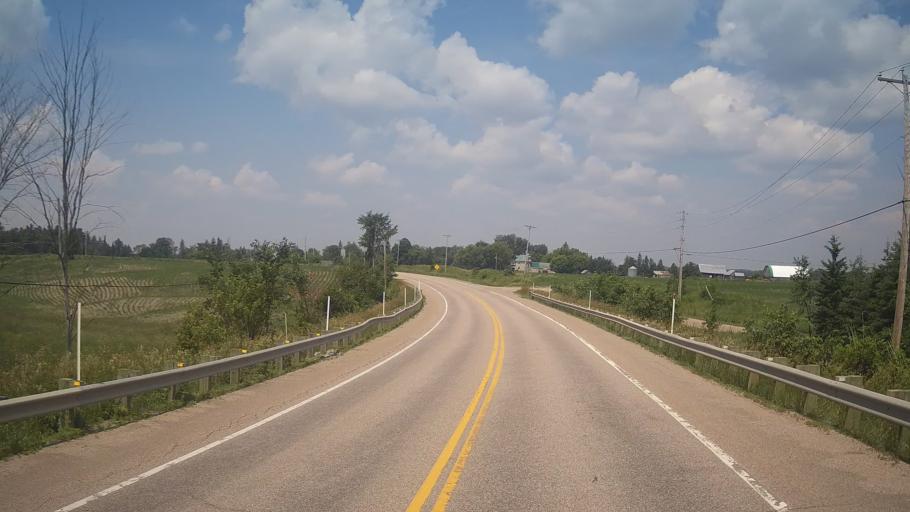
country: CA
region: Quebec
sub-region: Outaouais
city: Shawville
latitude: 45.5836
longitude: -76.4524
